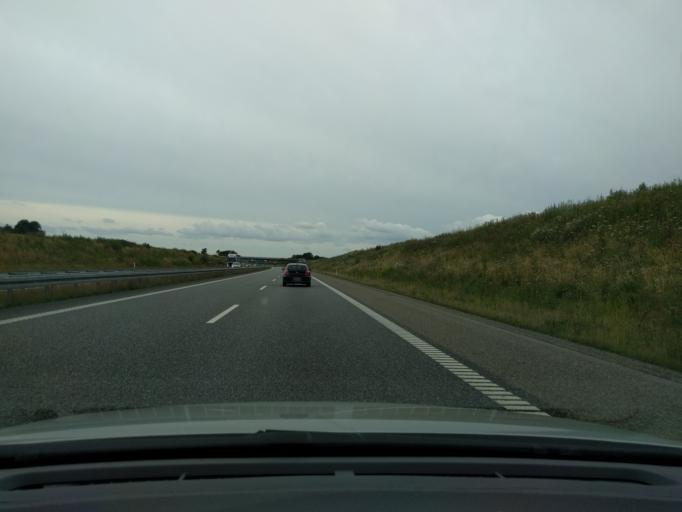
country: DK
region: Central Jutland
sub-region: Hedensted Kommune
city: Torring
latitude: 55.8162
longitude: 9.5502
